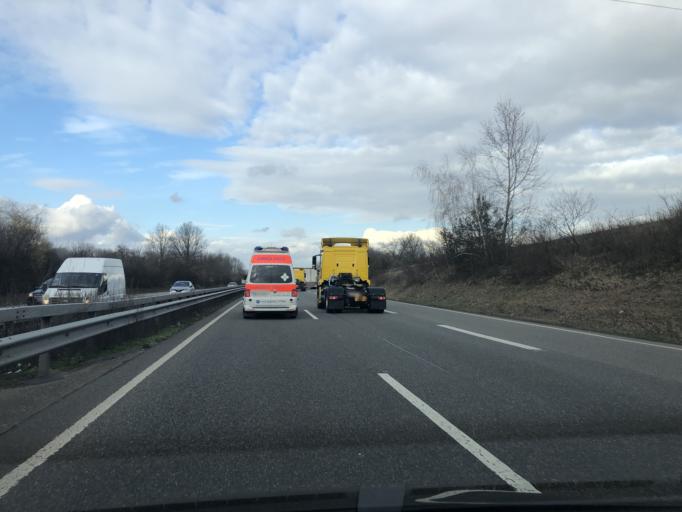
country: DE
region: Rheinland-Pfalz
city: Schwegenheim
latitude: 49.2642
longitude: 8.3349
